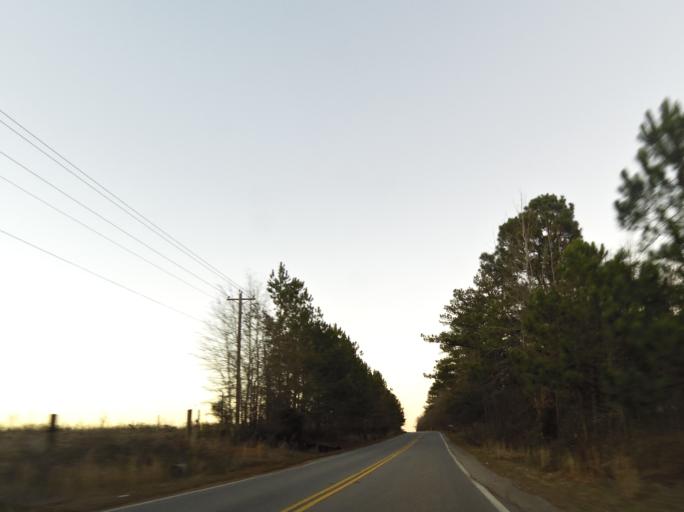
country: US
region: Georgia
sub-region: Peach County
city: Byron
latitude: 32.5876
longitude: -83.7483
